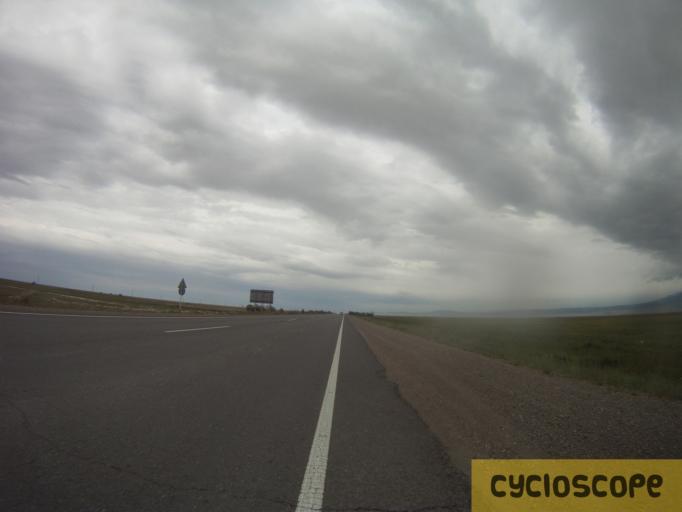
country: KZ
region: Zhambyl
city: Georgiyevka
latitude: 43.3971
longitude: 75.0698
